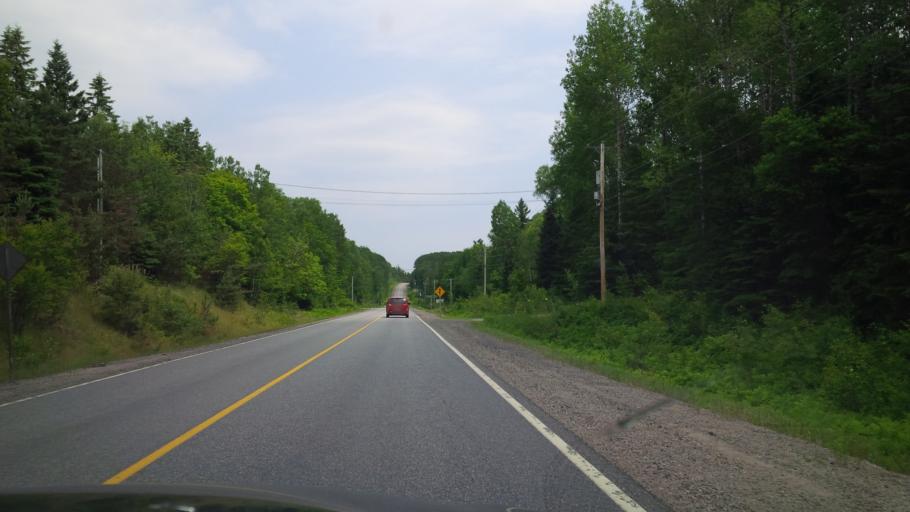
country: CA
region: Ontario
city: Huntsville
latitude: 45.5472
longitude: -79.2476
